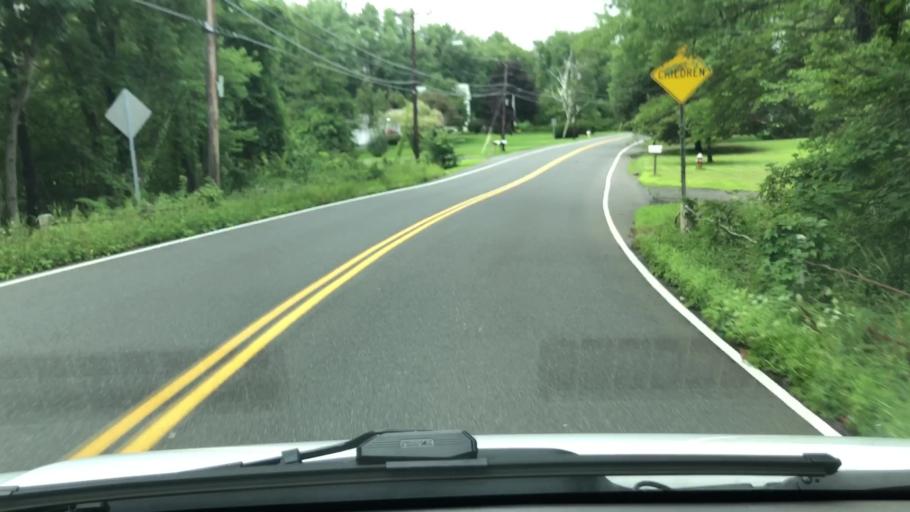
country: US
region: Massachusetts
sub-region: Franklin County
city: South Deerfield
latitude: 42.4956
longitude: -72.6087
